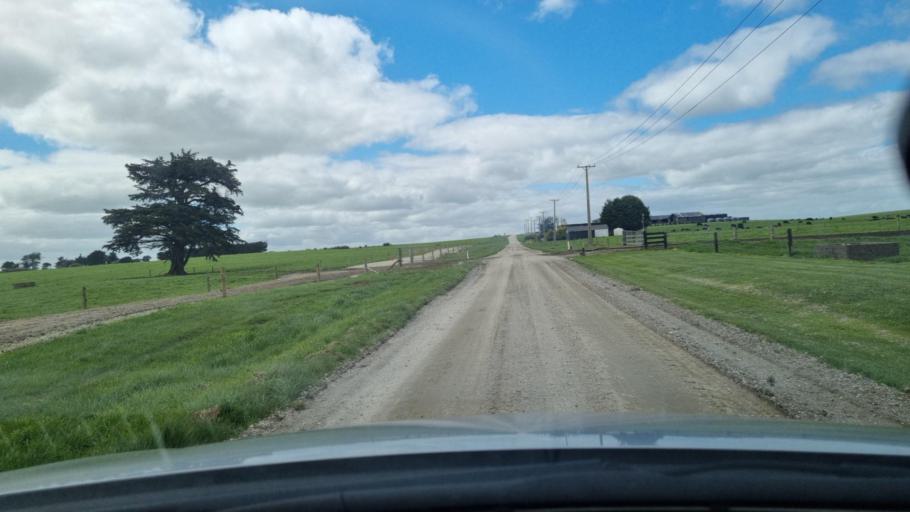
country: NZ
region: Southland
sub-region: Invercargill City
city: Invercargill
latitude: -46.4506
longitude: 168.4112
